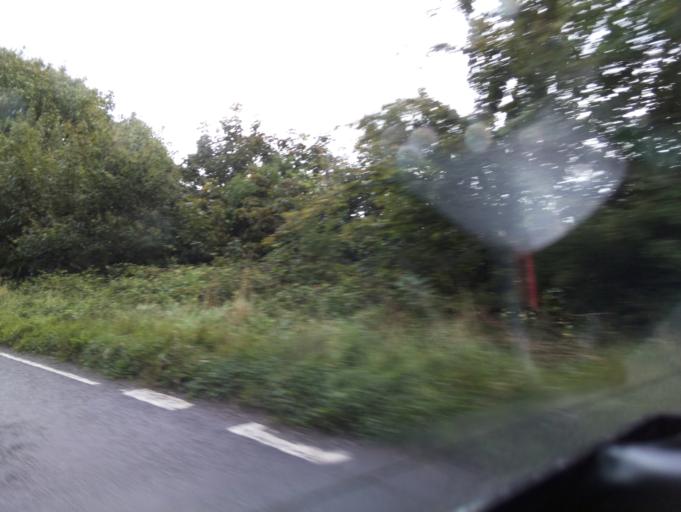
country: GB
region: England
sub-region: Devon
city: South Brent
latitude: 50.4164
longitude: -3.8385
